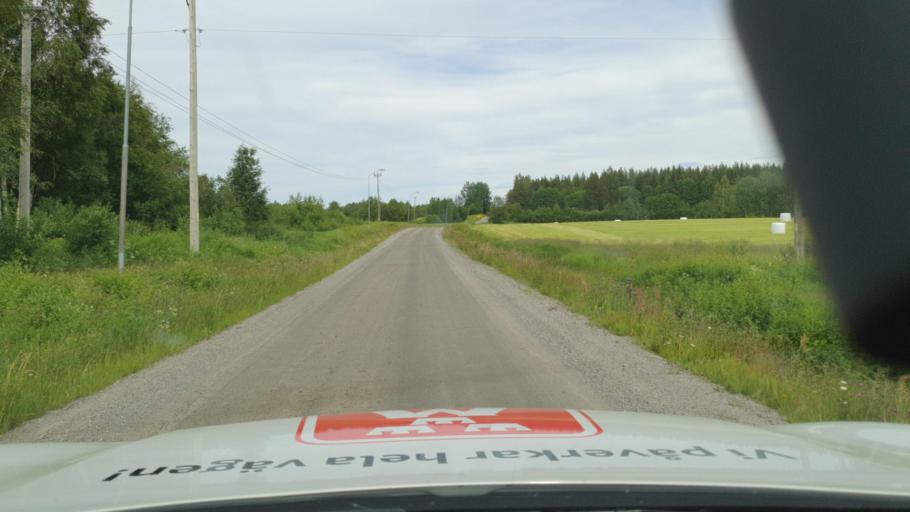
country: SE
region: Vaesterbotten
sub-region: Skelleftea Kommun
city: Viken
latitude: 64.5124
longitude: 20.9424
